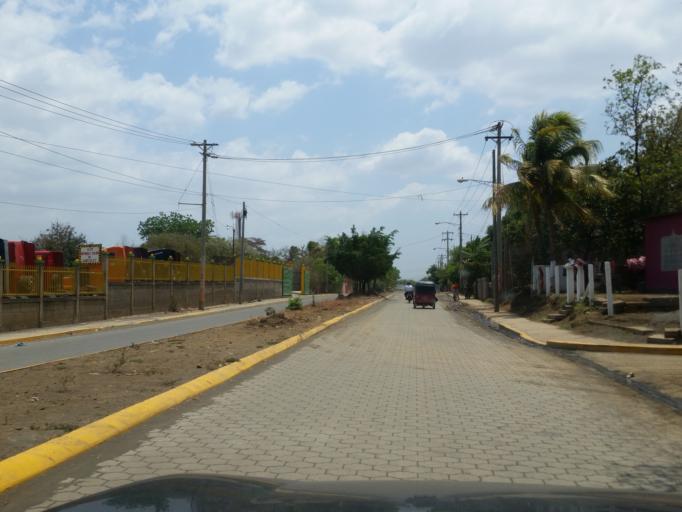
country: NI
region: Managua
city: Managua
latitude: 12.1354
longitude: -86.1844
